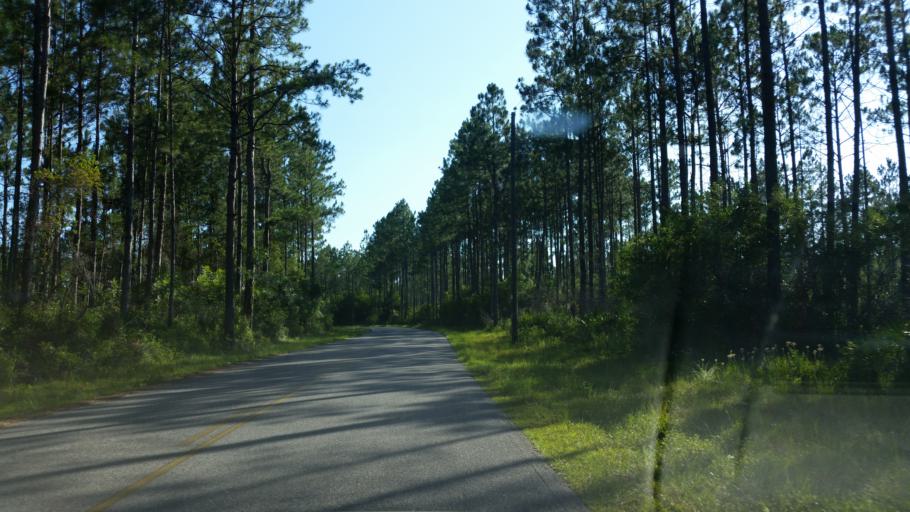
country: US
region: Florida
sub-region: Escambia County
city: Bellview
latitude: 30.4689
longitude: -87.4057
